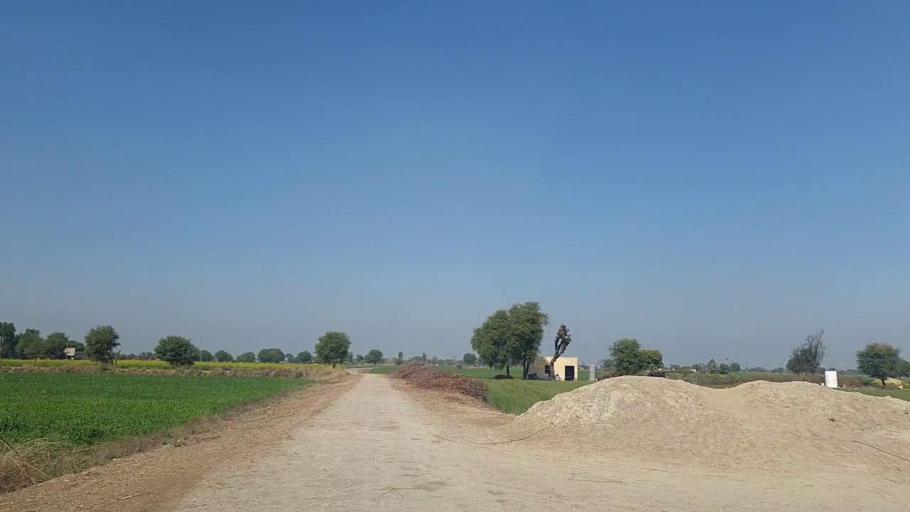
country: PK
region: Sindh
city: Shahpur Chakar
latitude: 26.1996
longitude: 68.5661
